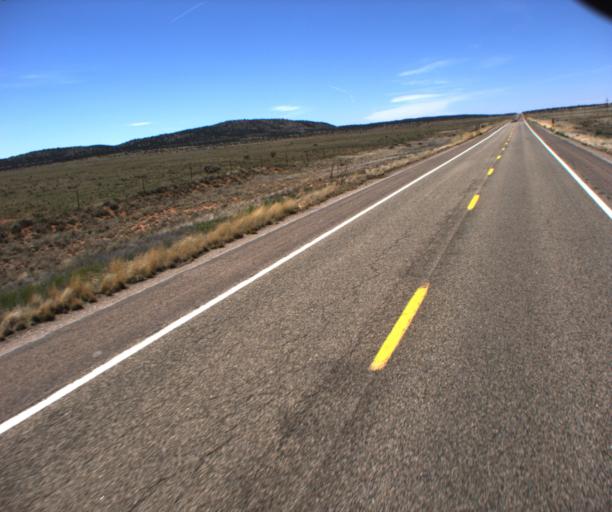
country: US
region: Arizona
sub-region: Mohave County
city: Peach Springs
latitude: 35.4790
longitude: -113.1388
